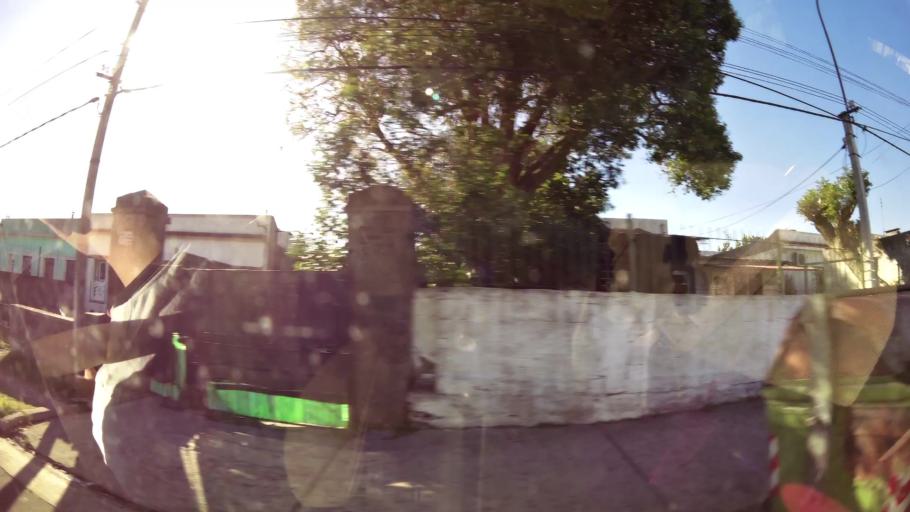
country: UY
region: Montevideo
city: Montevideo
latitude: -34.8448
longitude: -56.2331
